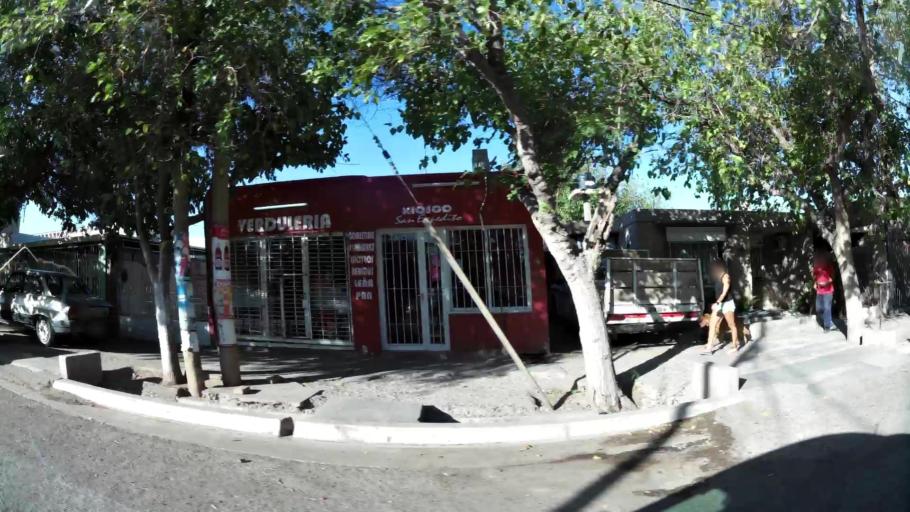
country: AR
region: San Juan
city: Villa Krause
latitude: -31.5572
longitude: -68.5158
